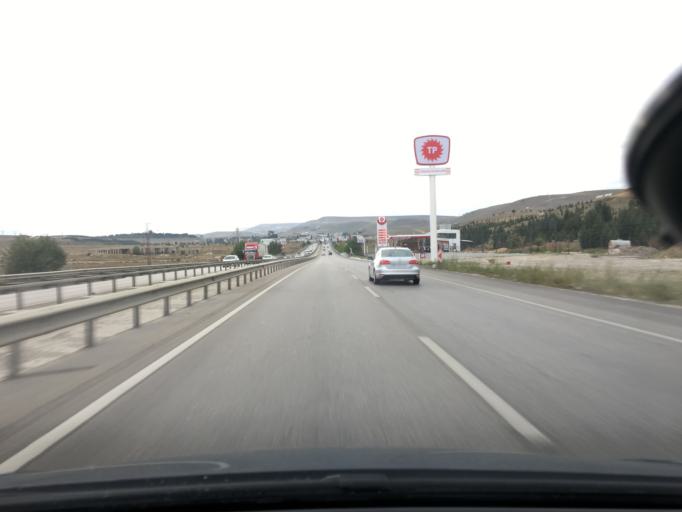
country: TR
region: Afyonkarahisar
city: Afyonkarahisar
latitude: 38.7924
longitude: 30.4139
